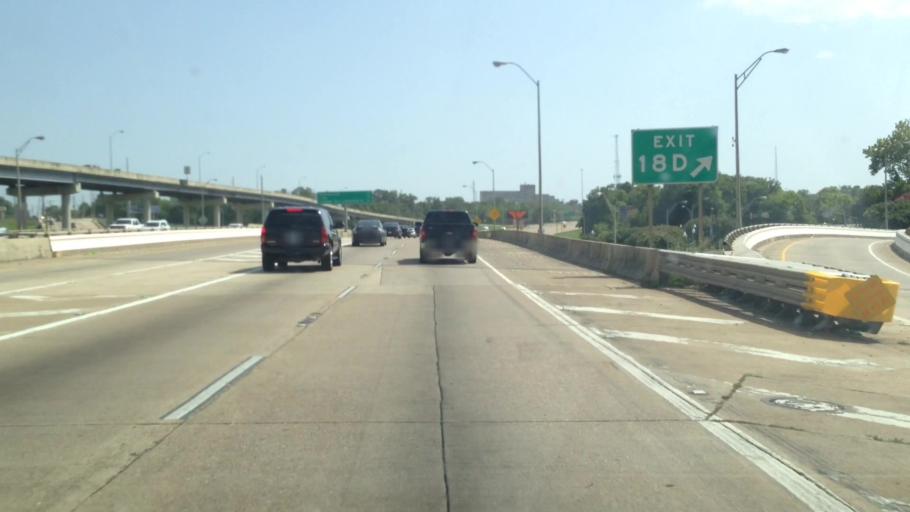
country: US
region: Louisiana
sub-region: Bossier Parish
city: Bossier City
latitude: 32.5066
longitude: -93.7461
